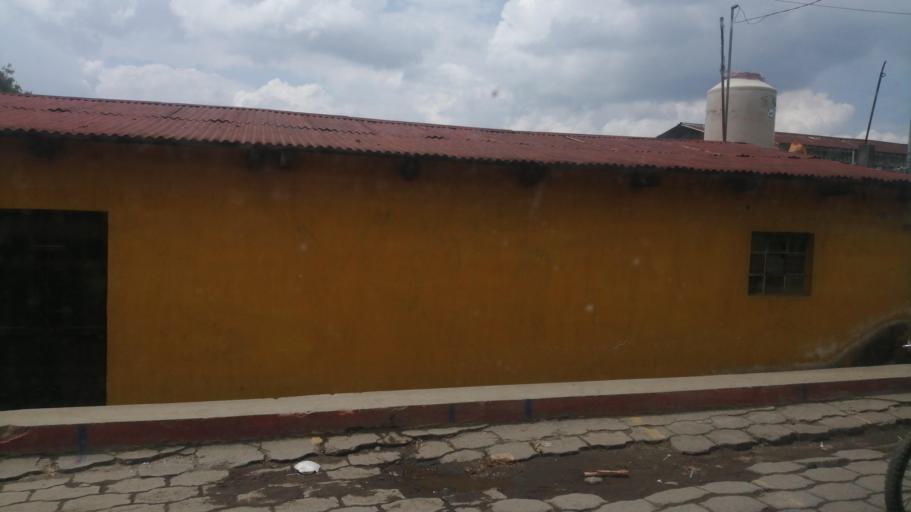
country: GT
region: Quetzaltenango
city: Cantel
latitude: 14.8197
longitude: -91.4336
